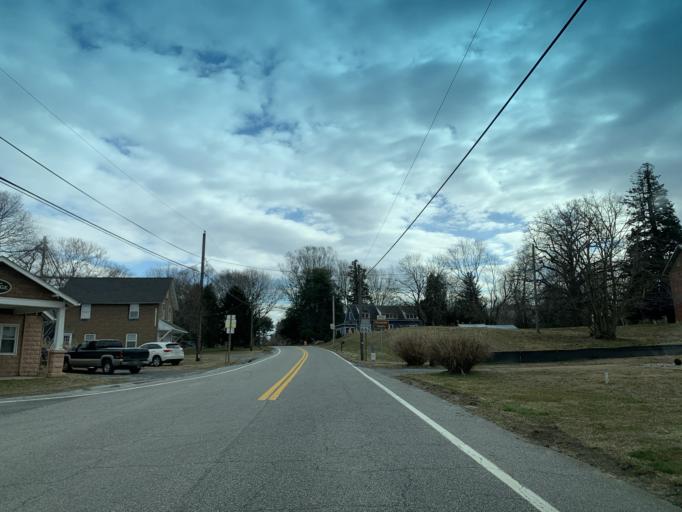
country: US
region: Maryland
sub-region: Queen Anne's County
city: Centreville
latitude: 38.9412
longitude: -76.0809
